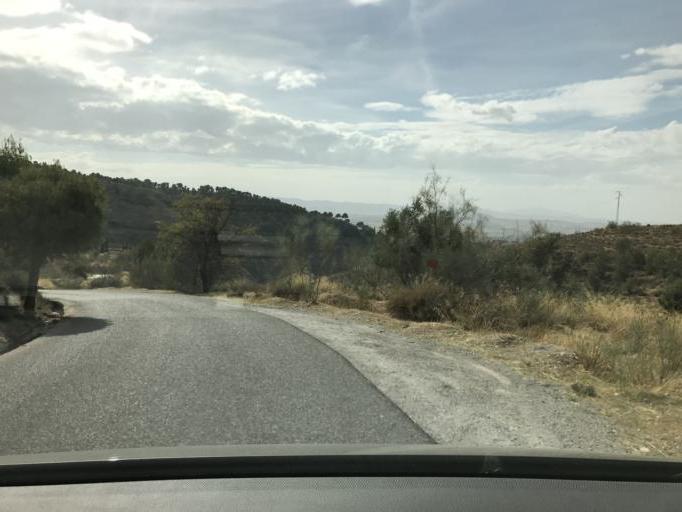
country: ES
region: Andalusia
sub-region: Provincia de Granada
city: Granada
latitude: 37.1870
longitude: -3.5771
